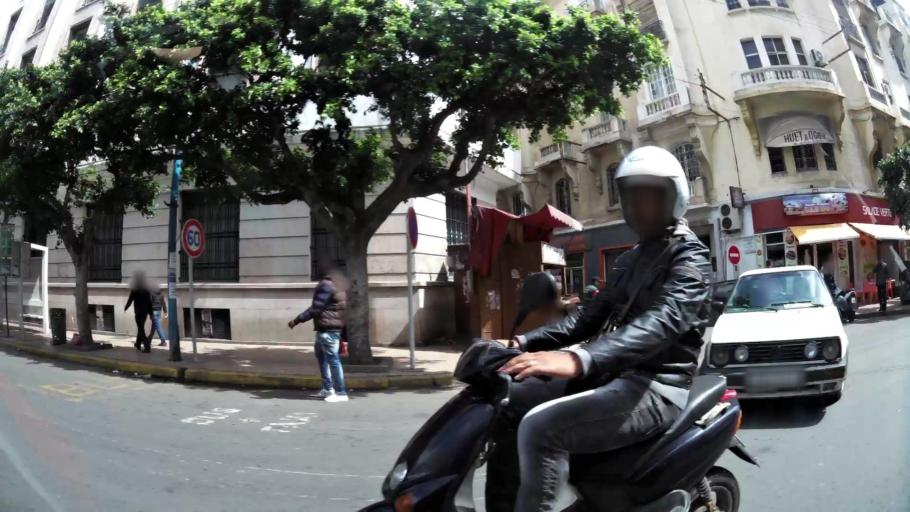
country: MA
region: Grand Casablanca
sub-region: Casablanca
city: Casablanca
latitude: 33.5918
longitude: -7.6153
